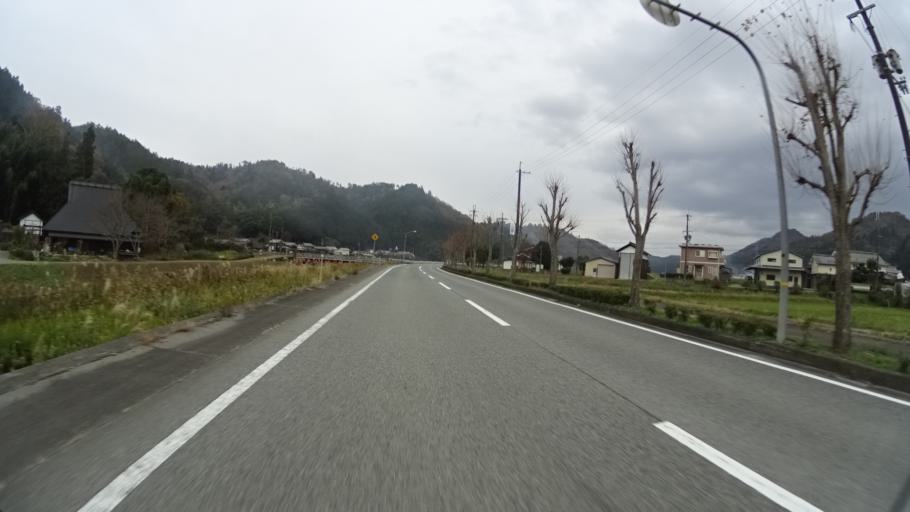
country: JP
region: Hyogo
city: Sasayama
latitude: 35.0736
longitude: 135.3504
